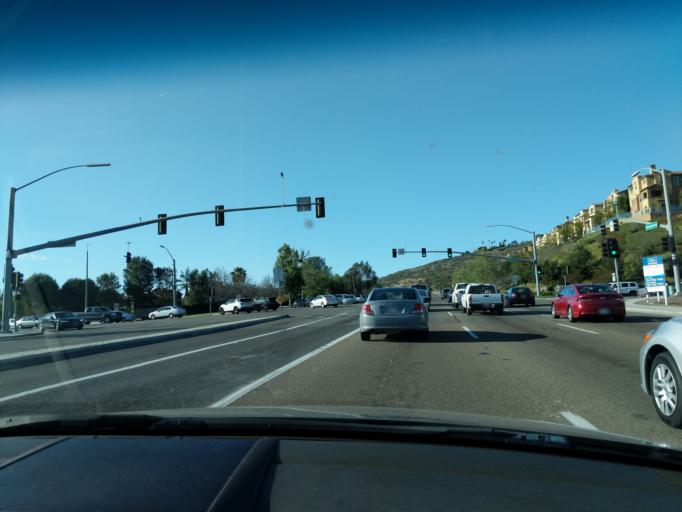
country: US
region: California
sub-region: San Diego County
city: Lake San Marcos
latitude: 33.1067
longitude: -117.2254
